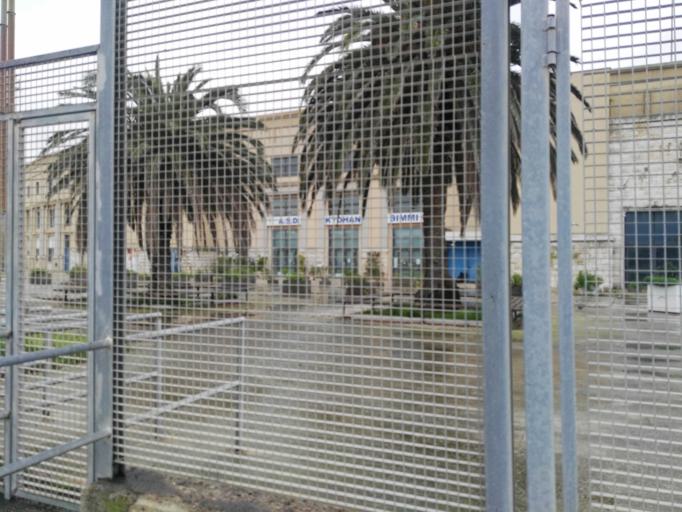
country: IT
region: Apulia
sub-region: Provincia di Bari
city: Bari
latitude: 41.1333
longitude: 16.8411
